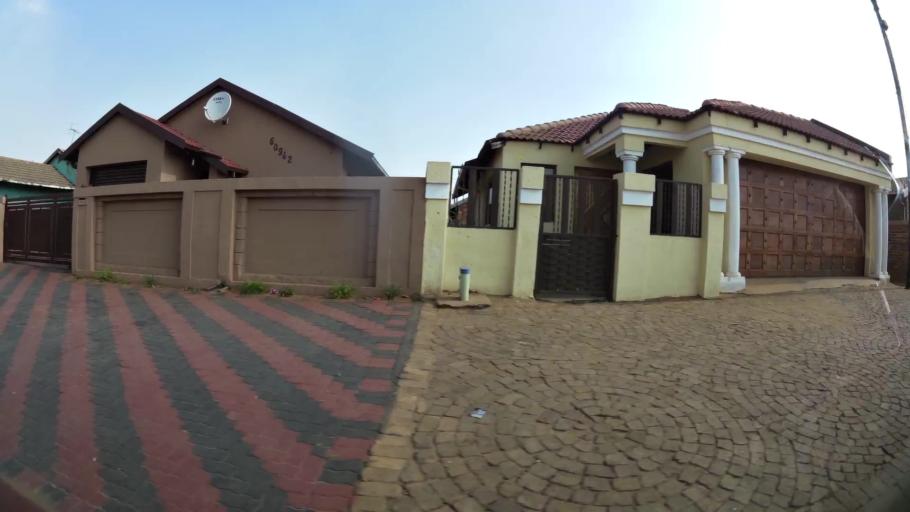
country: ZA
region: Gauteng
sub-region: Ekurhuleni Metropolitan Municipality
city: Brakpan
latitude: -26.1338
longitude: 28.4242
